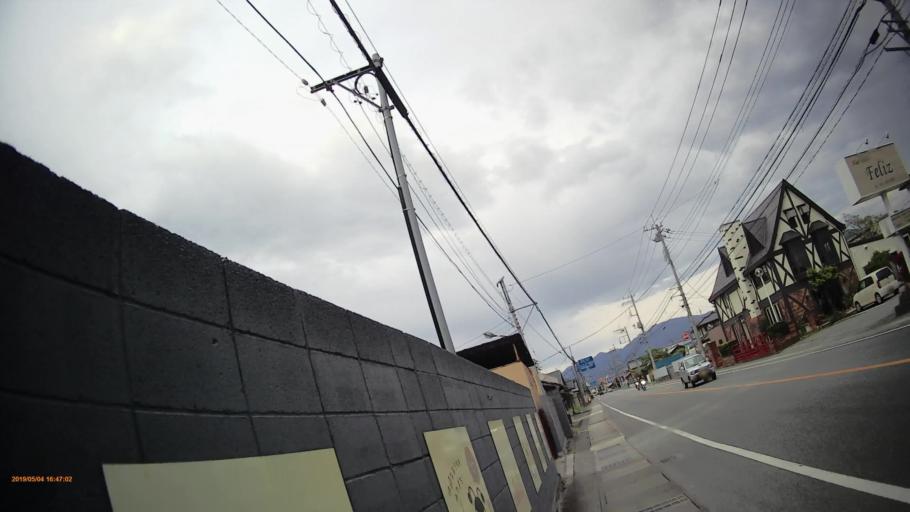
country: JP
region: Yamanashi
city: Isawa
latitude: 35.6547
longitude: 138.6099
